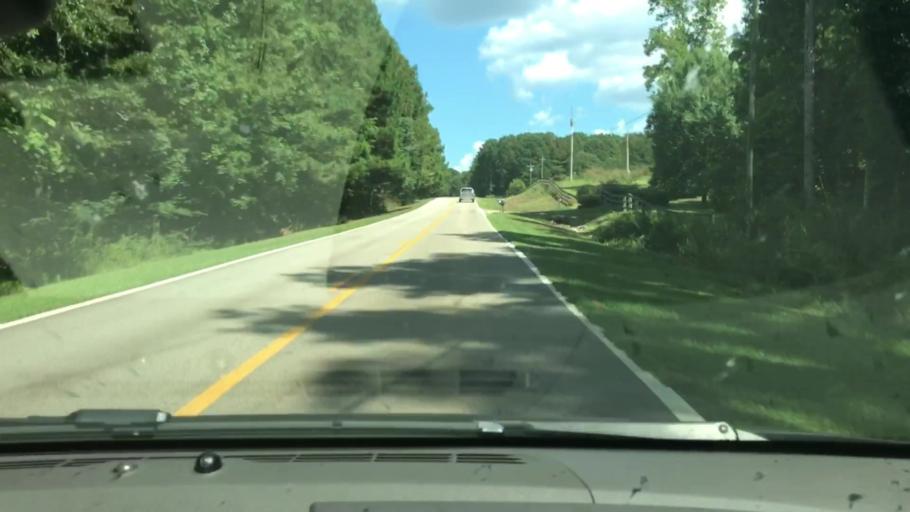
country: US
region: Georgia
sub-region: Troup County
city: La Grange
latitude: 33.1413
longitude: -85.0970
